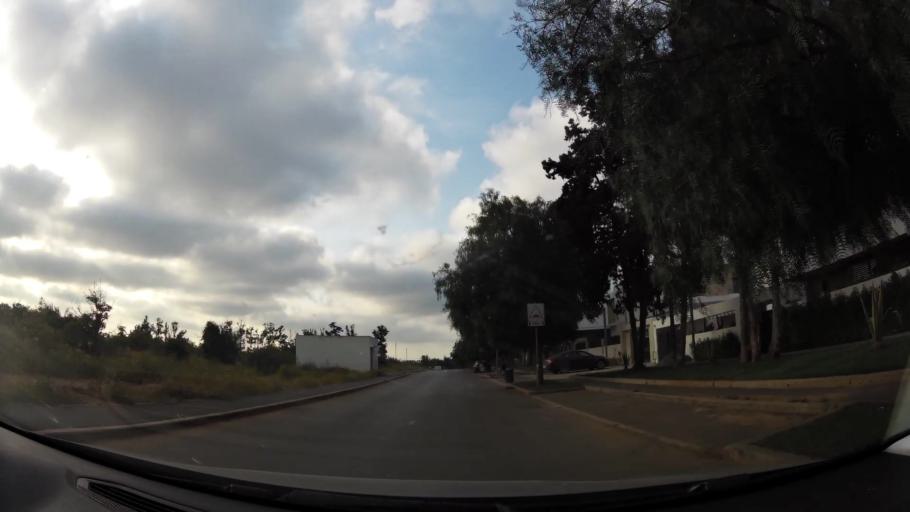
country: MA
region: Rabat-Sale-Zemmour-Zaer
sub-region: Rabat
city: Rabat
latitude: 33.9515
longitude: -6.8384
